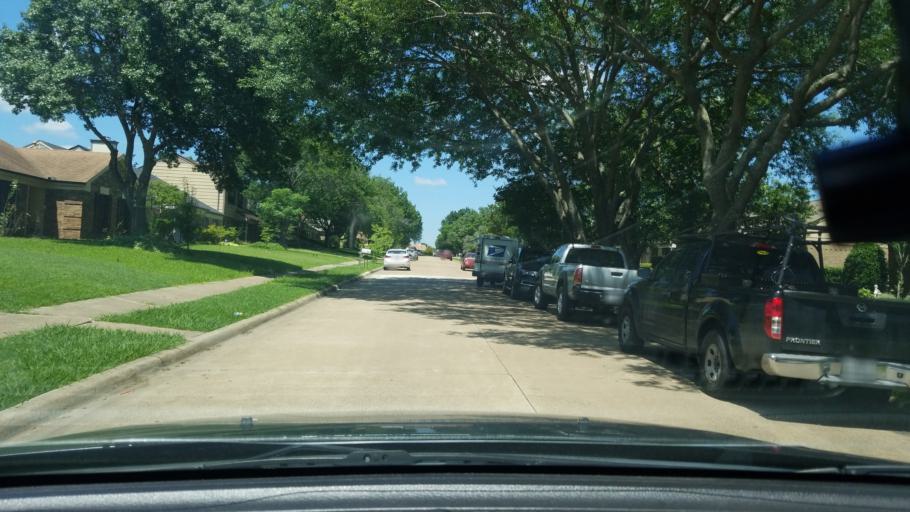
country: US
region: Texas
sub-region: Dallas County
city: Mesquite
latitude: 32.7945
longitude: -96.5984
